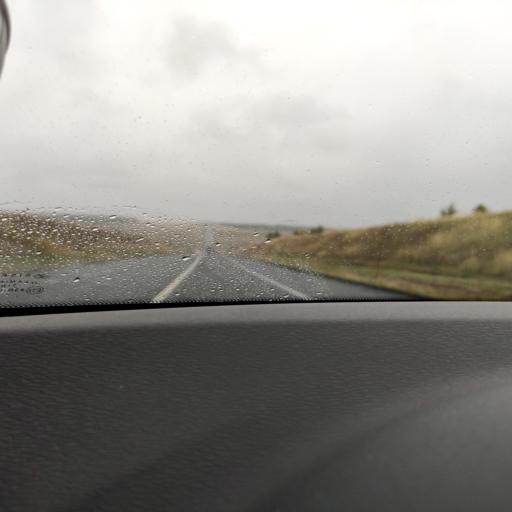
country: RU
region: Samara
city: Yelkhovka
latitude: 53.7317
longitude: 50.2311
